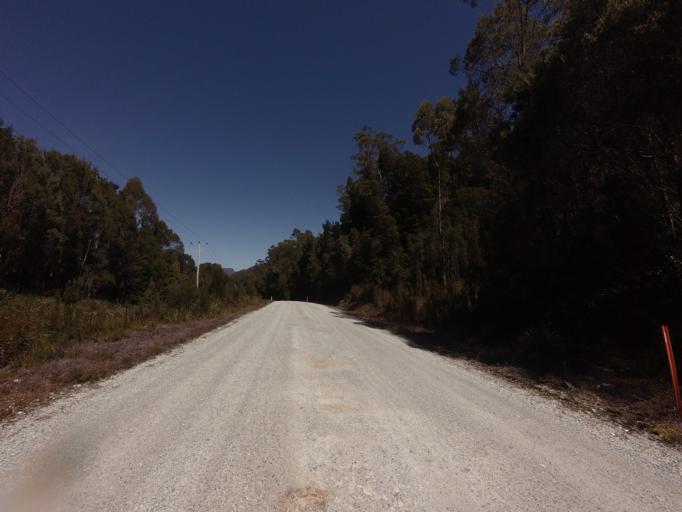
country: AU
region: Tasmania
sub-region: West Coast
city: Queenstown
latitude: -42.7585
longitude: 145.9854
